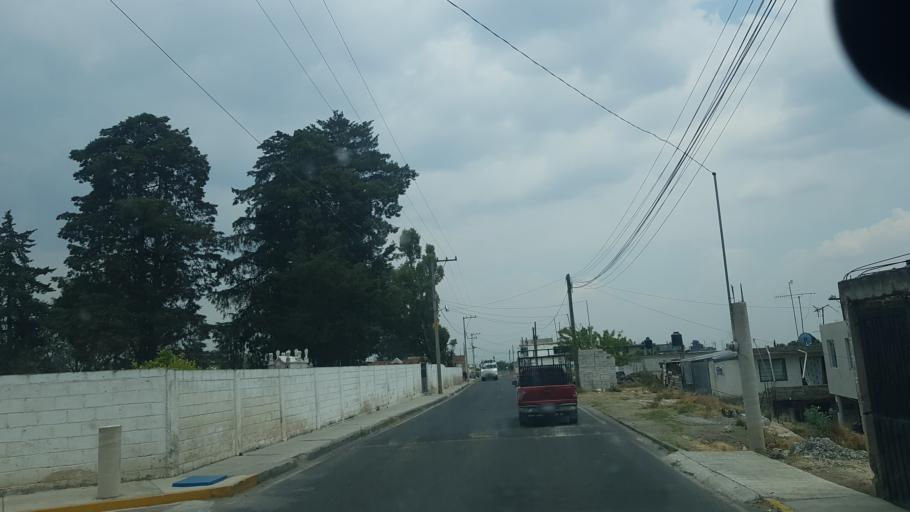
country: MX
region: Puebla
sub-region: Huejotzingo
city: San Mateo Capultitlan
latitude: 19.2010
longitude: -98.4377
